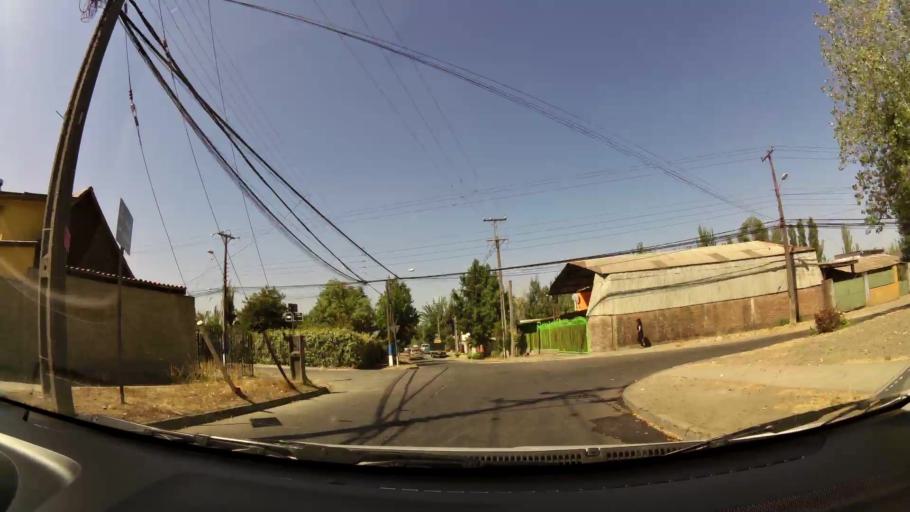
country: CL
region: Maule
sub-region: Provincia de Talca
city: Talca
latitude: -35.4162
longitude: -71.6474
